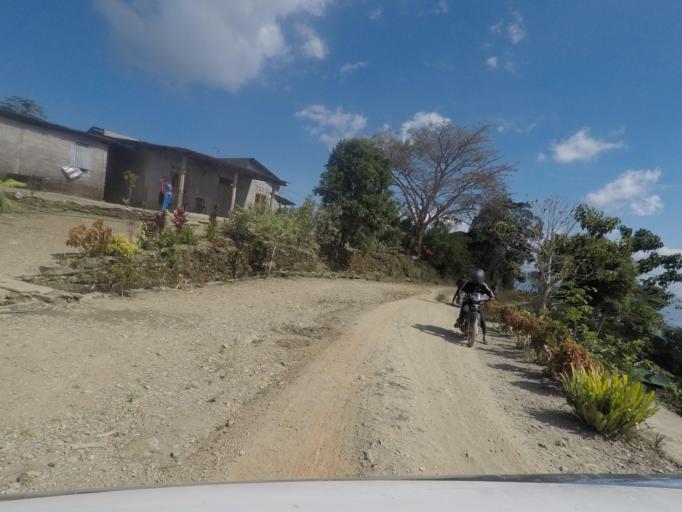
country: TL
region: Ermera
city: Gleno
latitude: -8.7530
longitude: 125.3239
